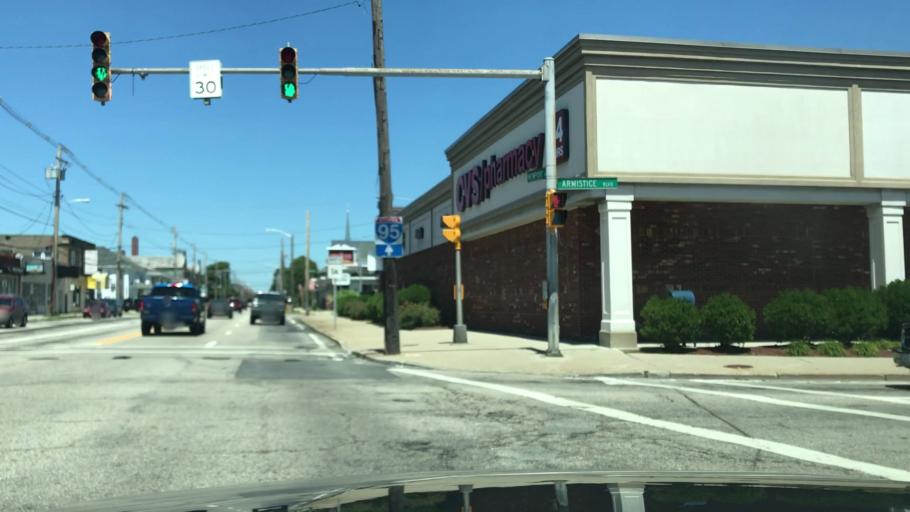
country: US
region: Massachusetts
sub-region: Bristol County
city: North Seekonk
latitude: 41.8783
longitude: -71.3542
